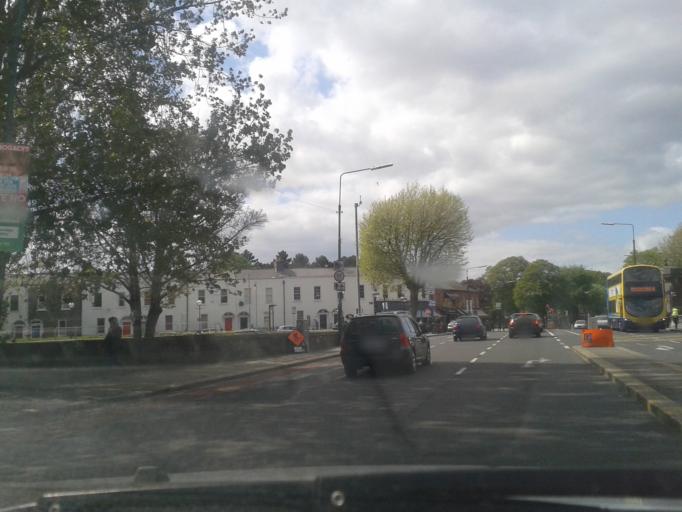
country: IE
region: Leinster
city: Ringsend
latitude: 53.3289
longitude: -6.2306
